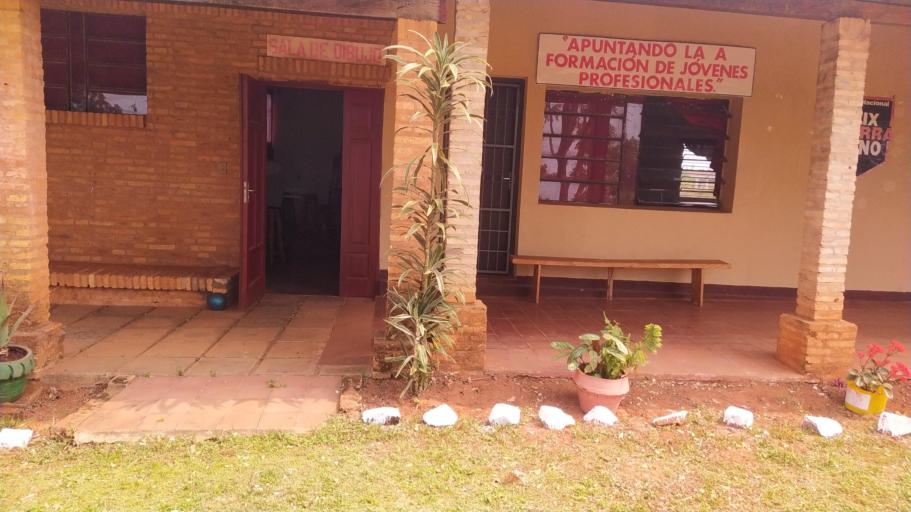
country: PY
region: Misiones
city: San Juan Bautista
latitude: -26.6723
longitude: -57.1191
